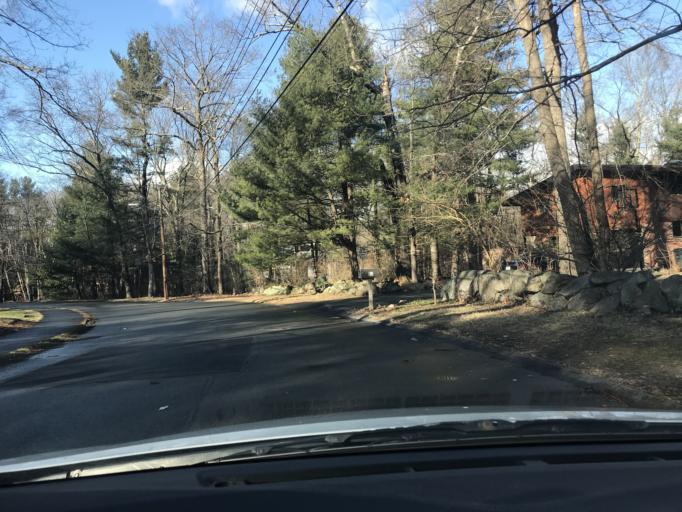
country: US
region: Massachusetts
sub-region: Middlesex County
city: Lexington
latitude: 42.4798
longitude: -71.2302
